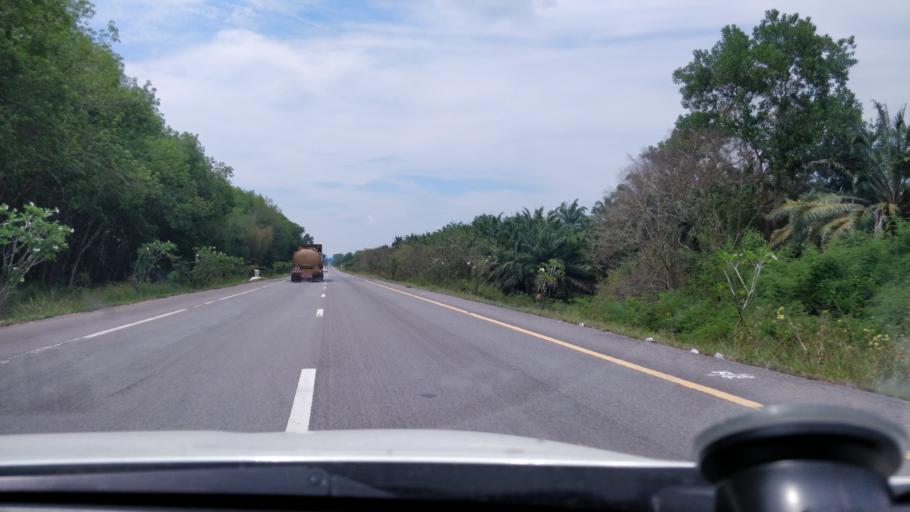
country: TH
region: Surat Thani
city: Khian Sa
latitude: 8.7575
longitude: 99.1610
